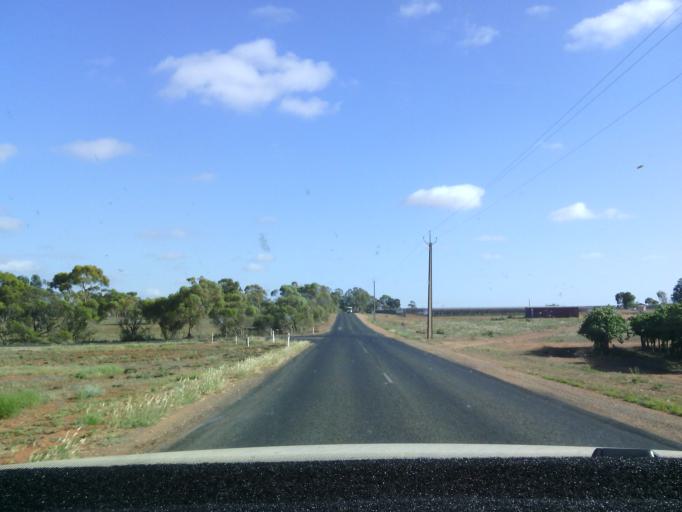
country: AU
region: South Australia
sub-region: Berri and Barmera
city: Monash
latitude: -34.2572
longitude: 140.5411
